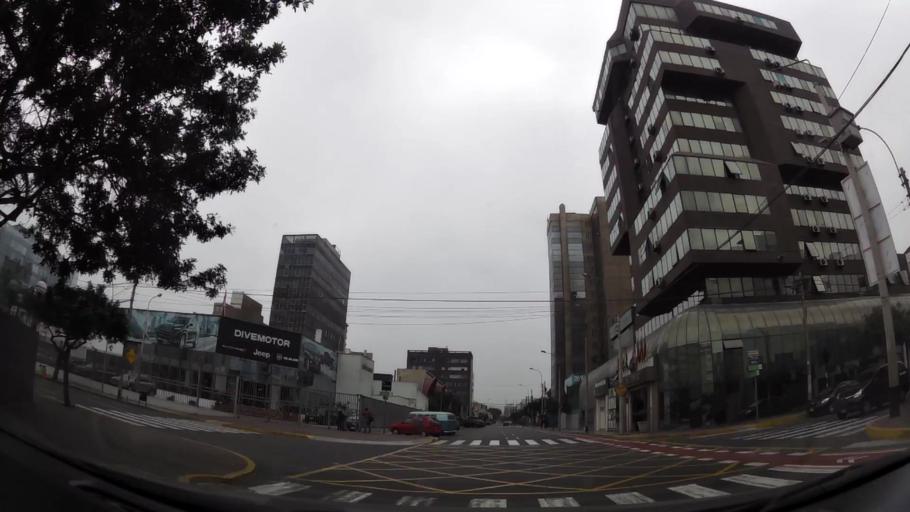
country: PE
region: Lima
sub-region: Lima
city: San Isidro
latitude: -12.1203
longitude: -77.0359
